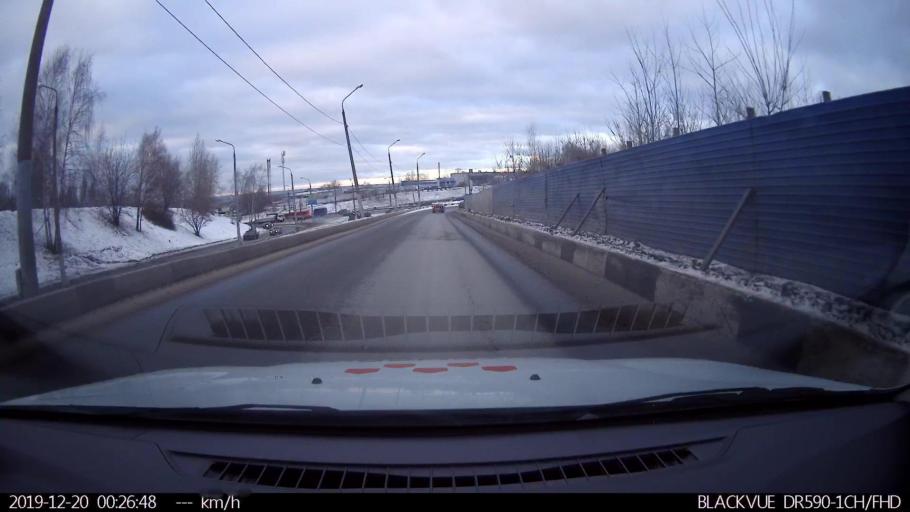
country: RU
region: Vladimir
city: Yur'yev-Pol'skiy
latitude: 56.6062
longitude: 39.5599
